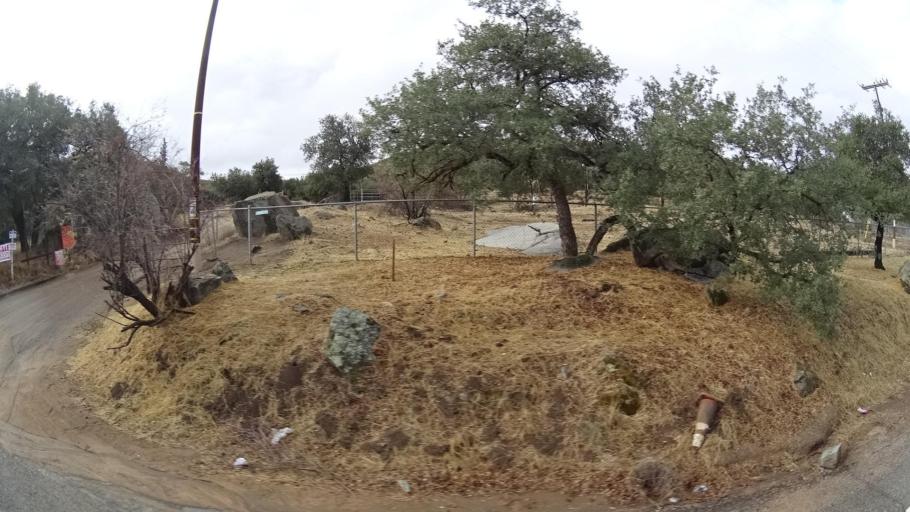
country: MX
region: Baja California
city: Tecate
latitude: 32.6053
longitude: -116.6146
